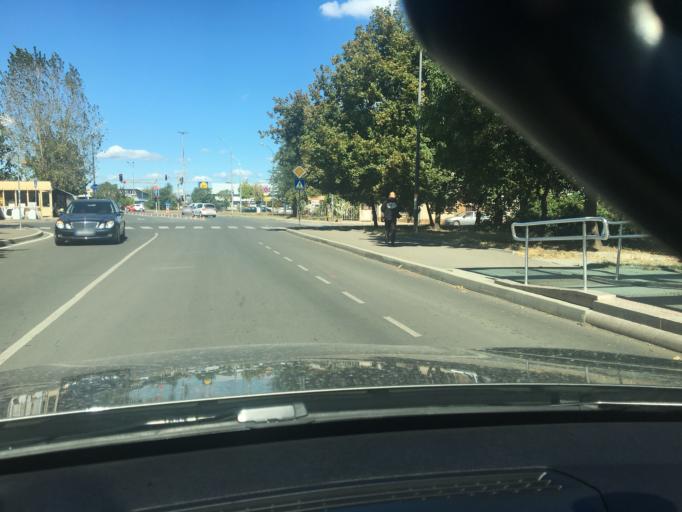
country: BG
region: Burgas
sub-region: Obshtina Burgas
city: Burgas
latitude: 42.5300
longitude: 27.4631
